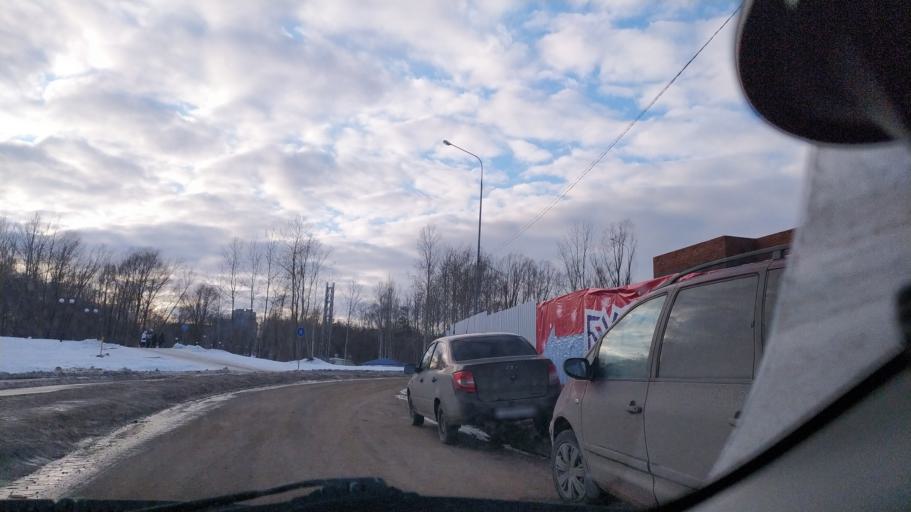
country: RU
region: Chuvashia
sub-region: Cheboksarskiy Rayon
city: Cheboksary
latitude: 56.1491
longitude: 47.2105
